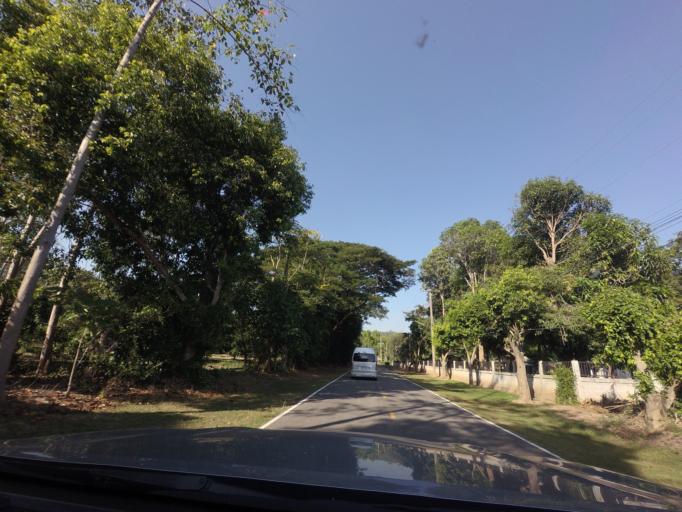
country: TH
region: Sukhothai
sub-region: Amphoe Si Satchanalai
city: Si Satchanalai
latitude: 17.4302
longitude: 99.7916
